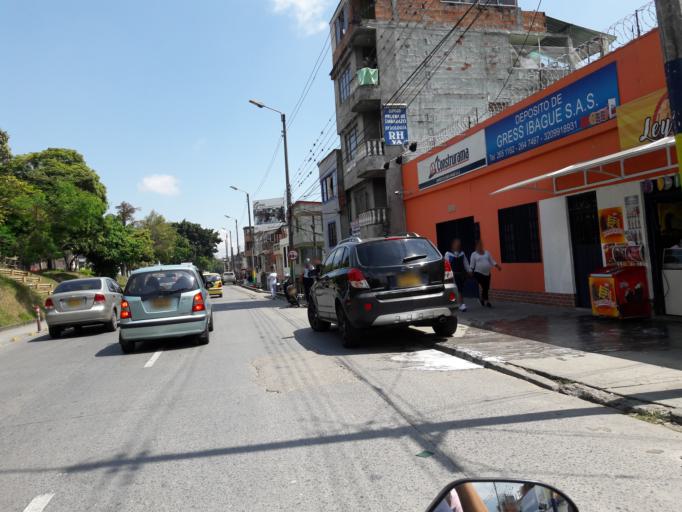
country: CO
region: Tolima
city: Ibague
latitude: 4.4349
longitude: -75.2190
